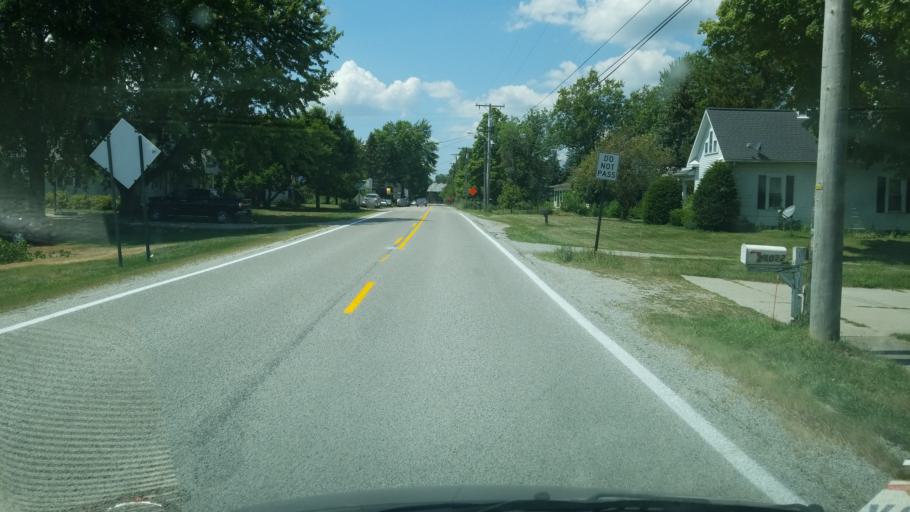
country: US
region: Ohio
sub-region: Champaign County
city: Mechanicsburg
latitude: 40.1217
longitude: -83.4872
